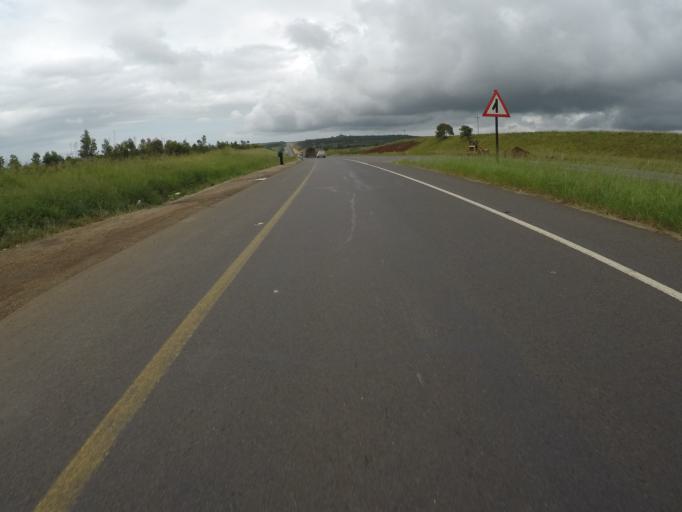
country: ZA
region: KwaZulu-Natal
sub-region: uThungulu District Municipality
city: Empangeni
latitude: -28.7721
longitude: 31.9299
